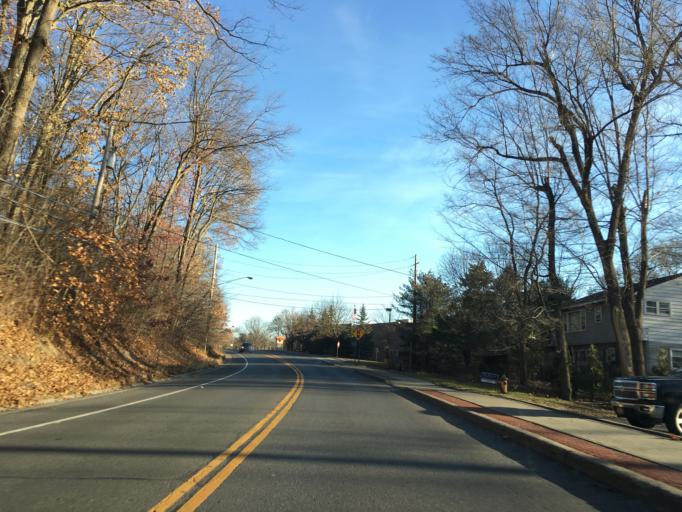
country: US
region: New York
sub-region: Rensselaer County
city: Wynantskill
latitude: 42.6987
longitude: -73.6510
